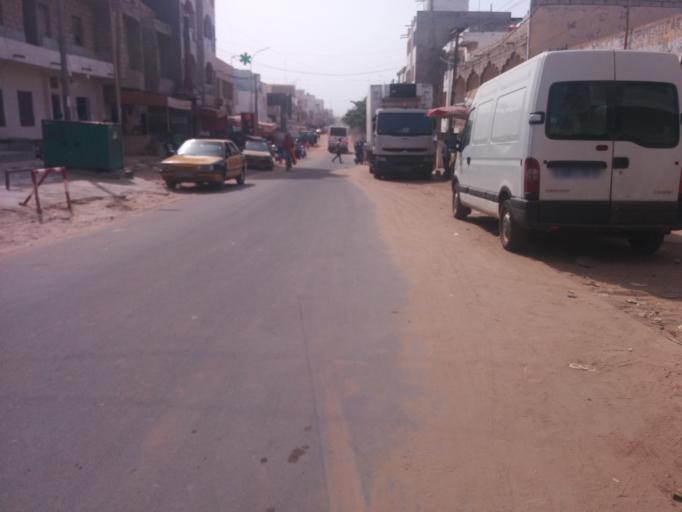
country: SN
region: Dakar
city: Pikine
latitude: 14.7645
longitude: -17.4386
